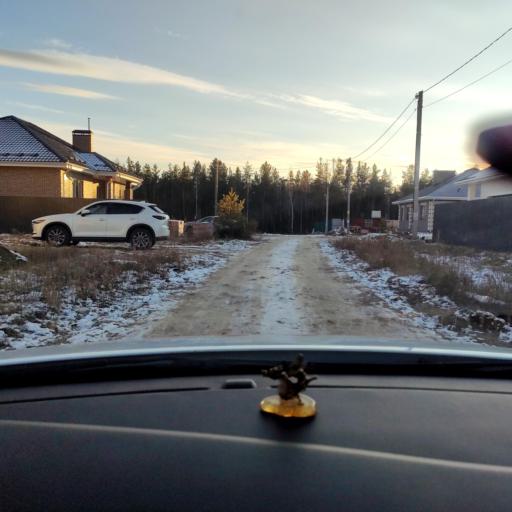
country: RU
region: Tatarstan
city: Stolbishchi
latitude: 55.6042
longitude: 49.1404
